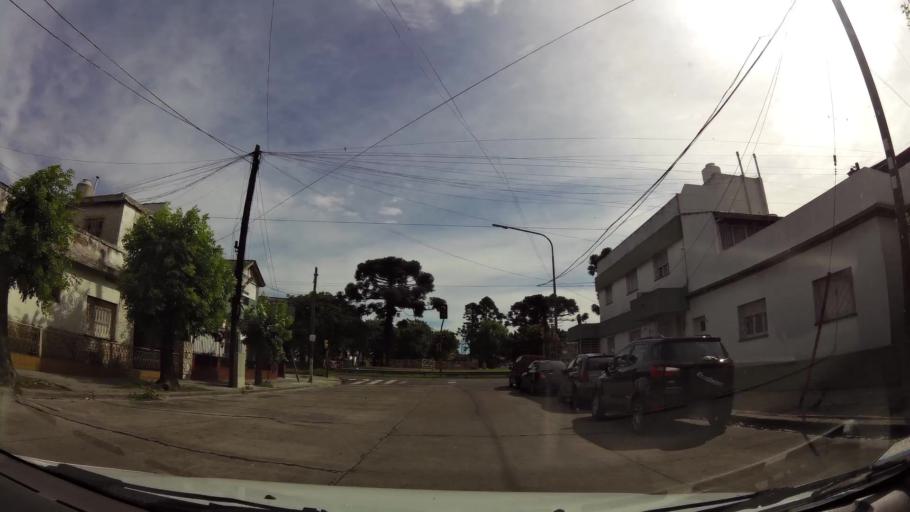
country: AR
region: Buenos Aires F.D.
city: Villa Lugano
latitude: -34.6666
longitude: -58.5110
